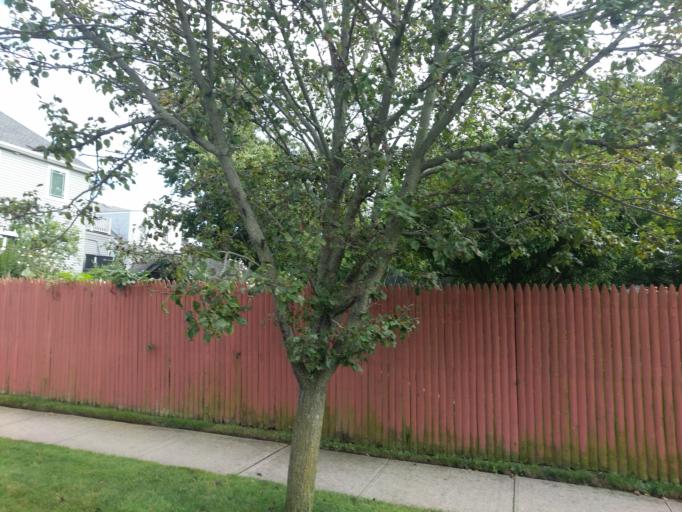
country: US
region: New York
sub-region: Nassau County
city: Cedarhurst
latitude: 40.6289
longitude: -73.7309
